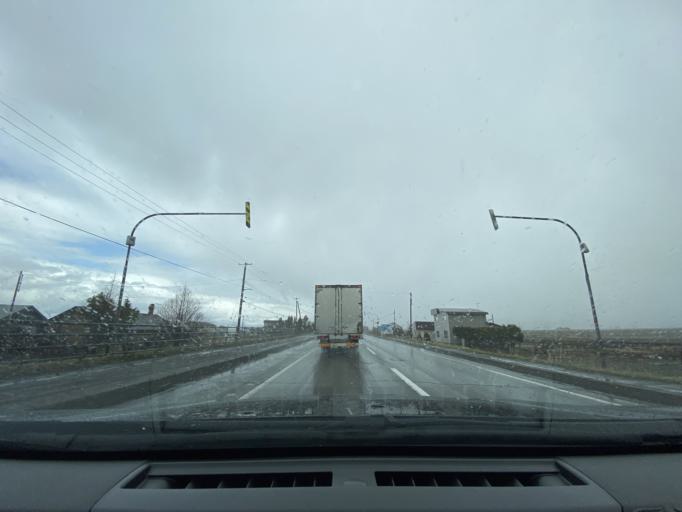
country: JP
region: Hokkaido
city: Fukagawa
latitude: 43.6572
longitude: 141.9839
